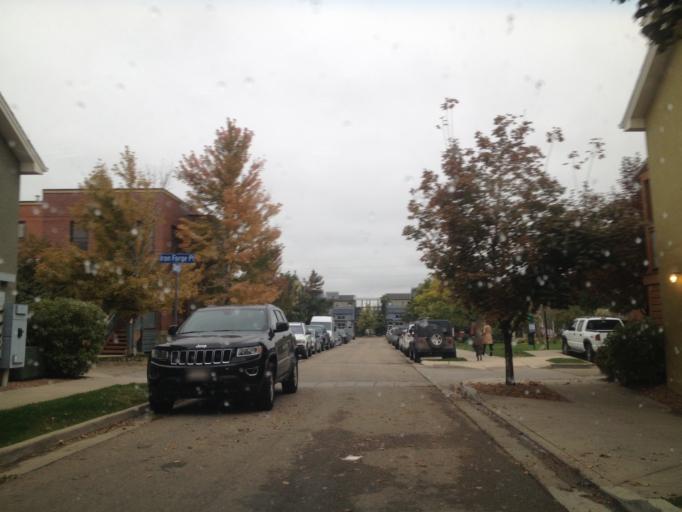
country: US
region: Colorado
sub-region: Boulder County
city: Boulder
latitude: 40.0275
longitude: -105.2521
